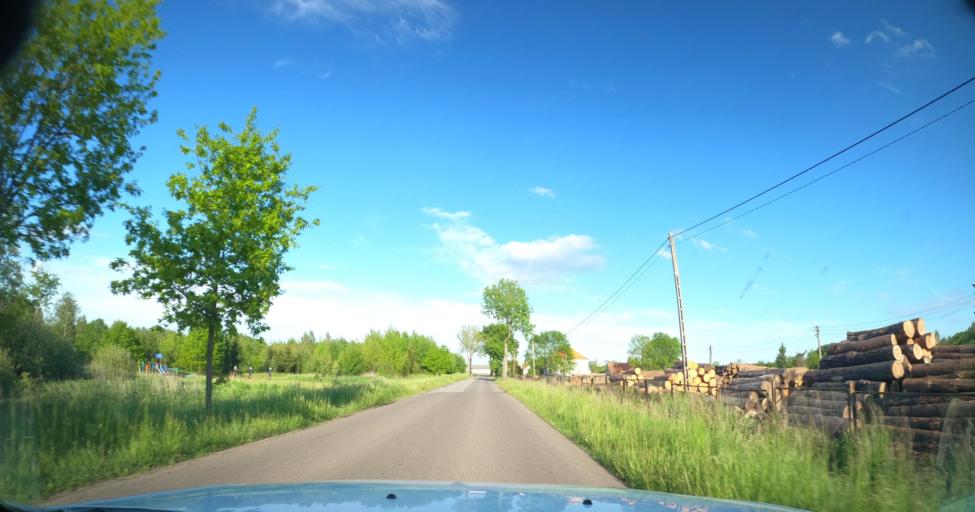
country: PL
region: Warmian-Masurian Voivodeship
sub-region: Powiat braniewski
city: Braniewo
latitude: 54.2735
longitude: 19.8030
